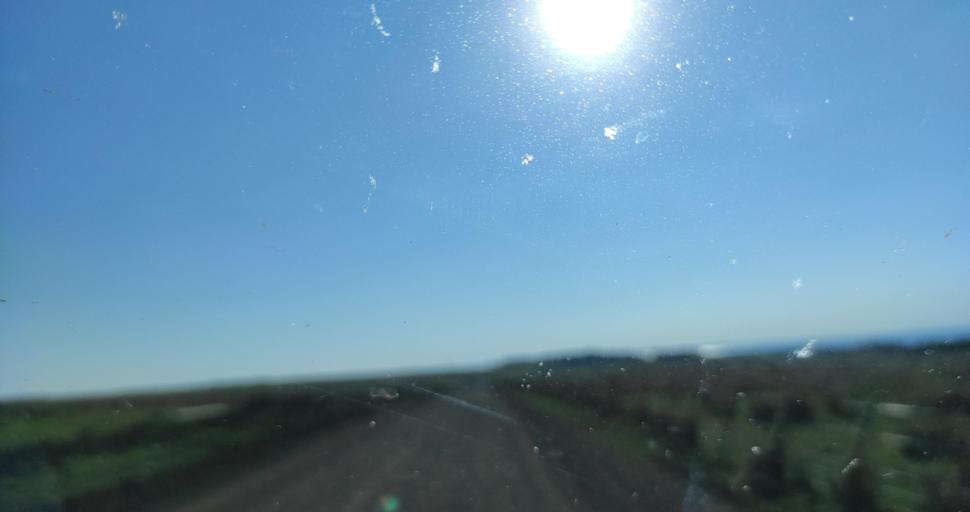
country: PY
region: Itapua
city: Carmen del Parana
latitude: -27.4145
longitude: -56.1359
